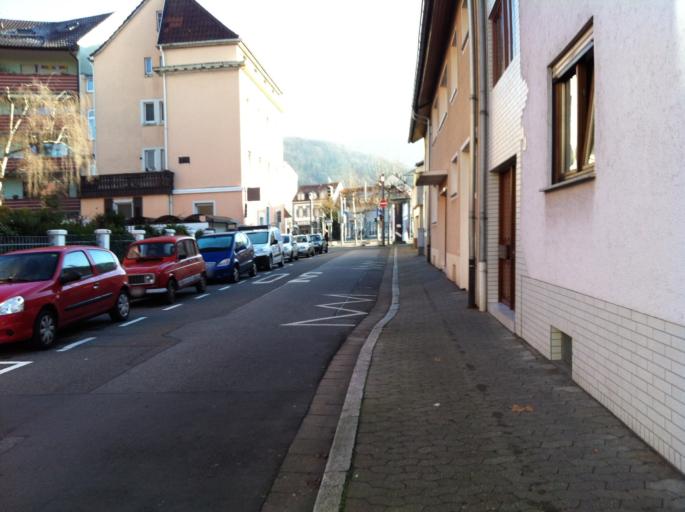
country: DE
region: Baden-Wuerttemberg
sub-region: Karlsruhe Region
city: Heidelberg
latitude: 49.3806
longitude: 8.6862
